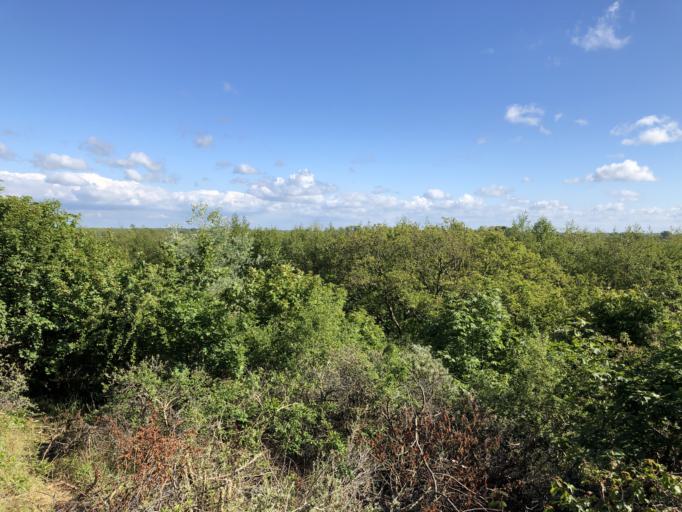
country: NL
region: South Holland
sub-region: Gemeente Wassenaar
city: Wassenaar
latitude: 52.1732
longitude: 4.3944
